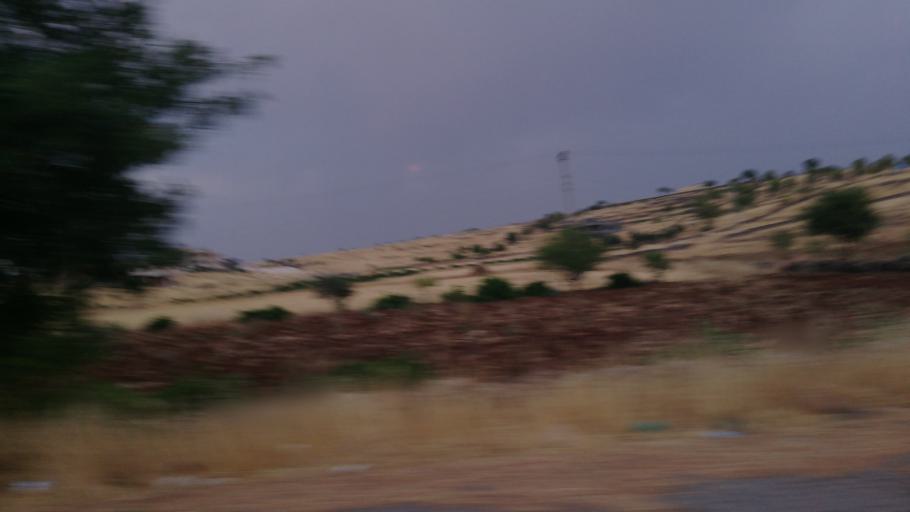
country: TR
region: Mardin
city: Kindirip
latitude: 37.4566
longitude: 41.2239
